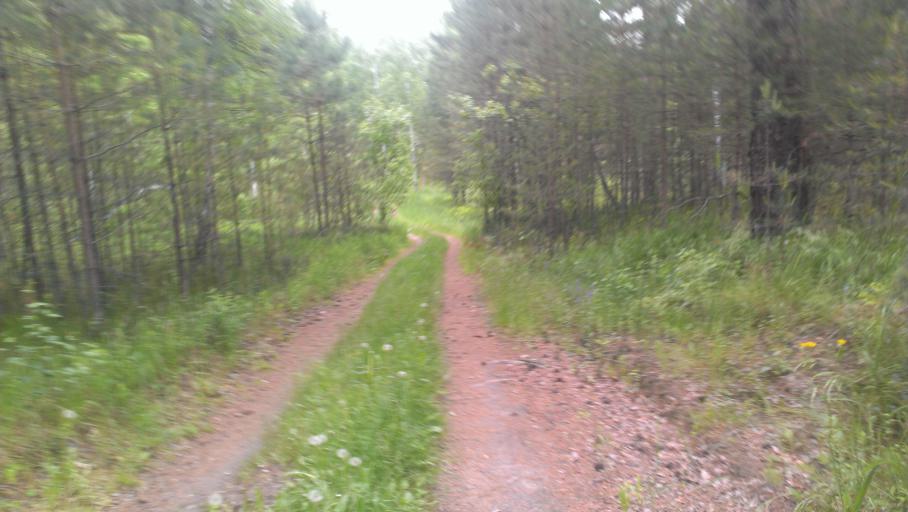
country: RU
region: Altai Krai
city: Sannikovo
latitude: 53.3487
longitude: 84.0385
